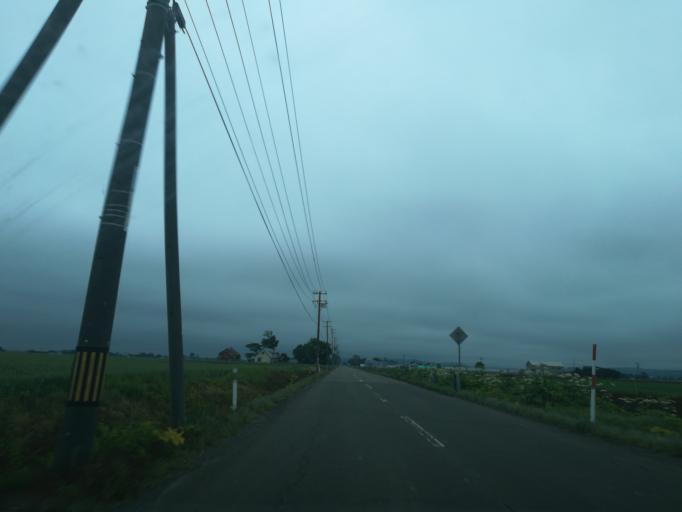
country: JP
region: Hokkaido
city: Iwamizawa
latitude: 43.1312
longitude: 141.7010
